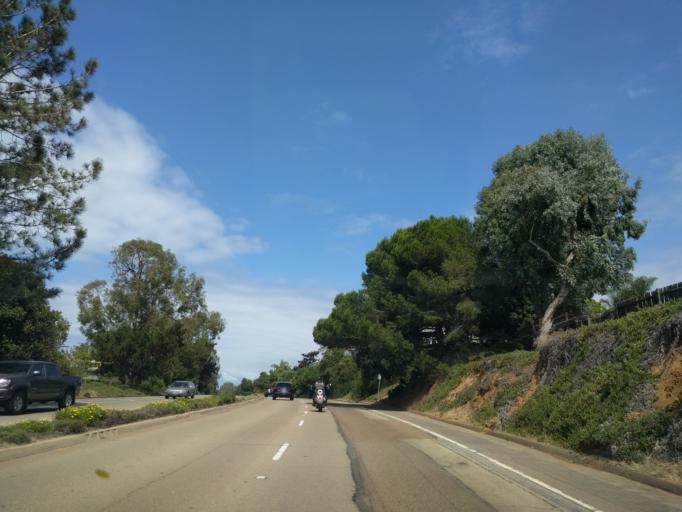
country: US
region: California
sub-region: San Diego County
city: Del Mar
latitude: 32.9457
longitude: -117.2601
